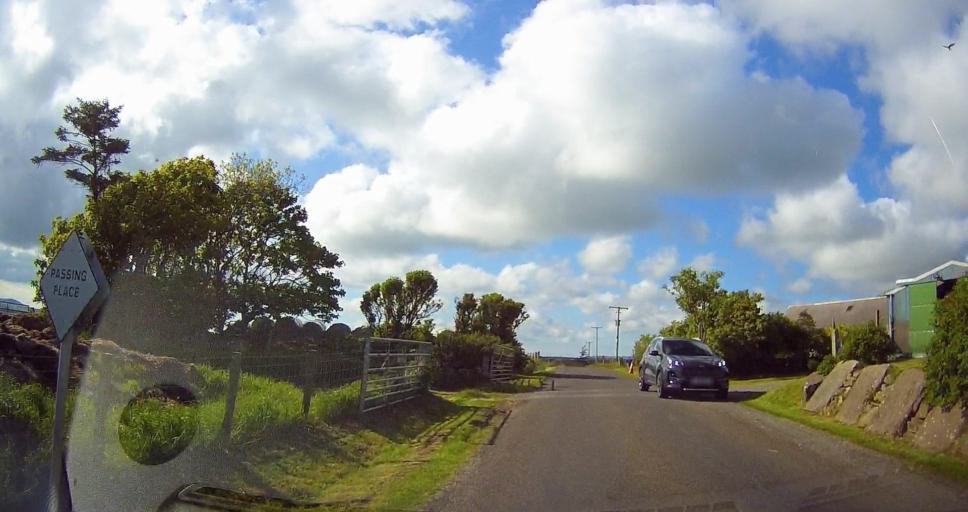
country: GB
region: Scotland
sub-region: Orkney Islands
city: Stromness
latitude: 58.9931
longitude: -3.1577
